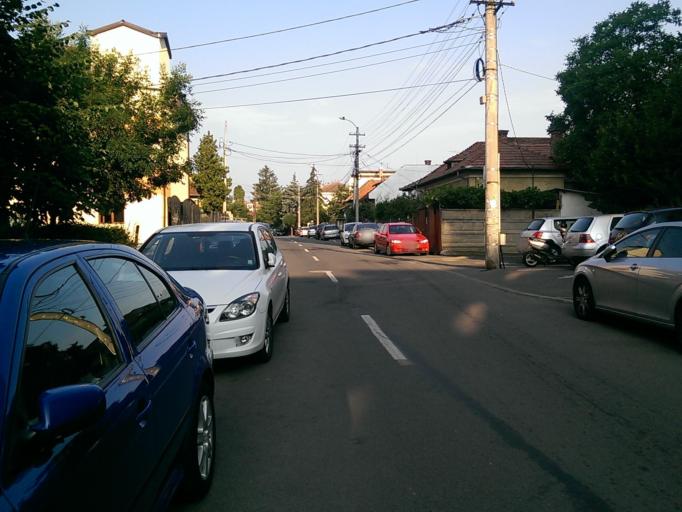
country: RO
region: Cluj
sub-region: Municipiul Cluj-Napoca
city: Cluj-Napoca
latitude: 46.7685
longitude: 23.6159
